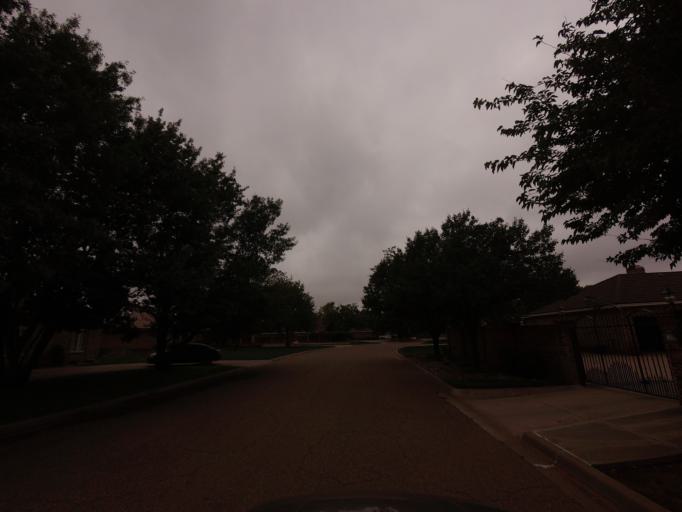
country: US
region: New Mexico
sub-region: Curry County
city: Clovis
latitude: 34.4270
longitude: -103.1798
